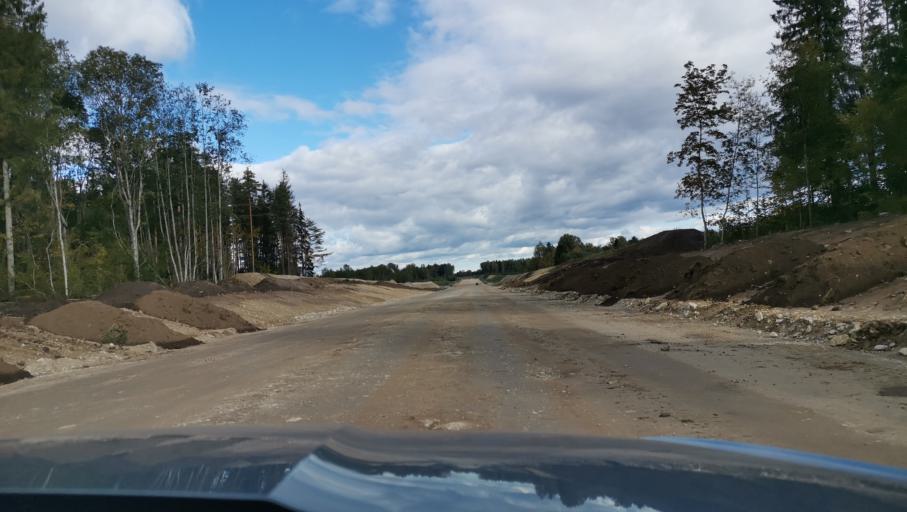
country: EE
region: Harju
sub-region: Keila linn
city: Keila
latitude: 59.1401
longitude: 24.4893
